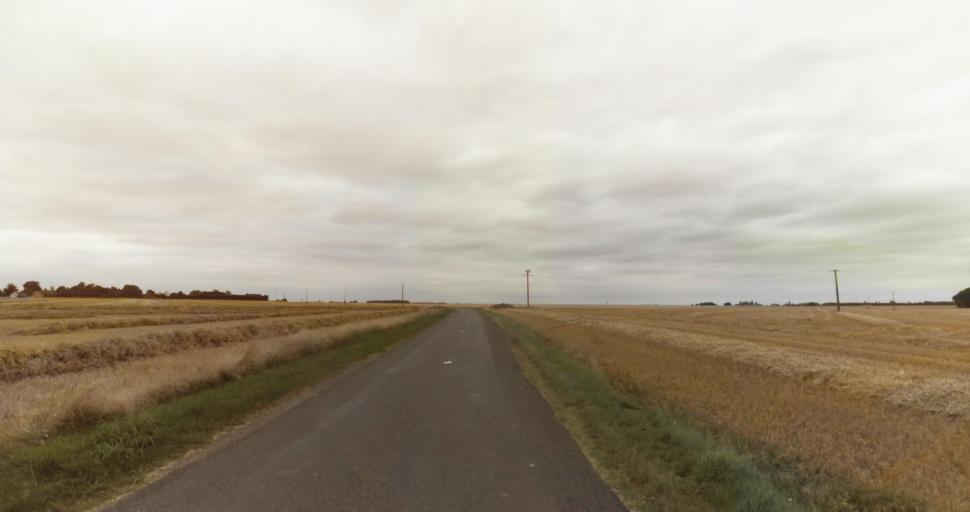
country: FR
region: Haute-Normandie
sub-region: Departement de l'Eure
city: Marcilly-sur-Eure
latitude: 48.9375
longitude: 1.2688
